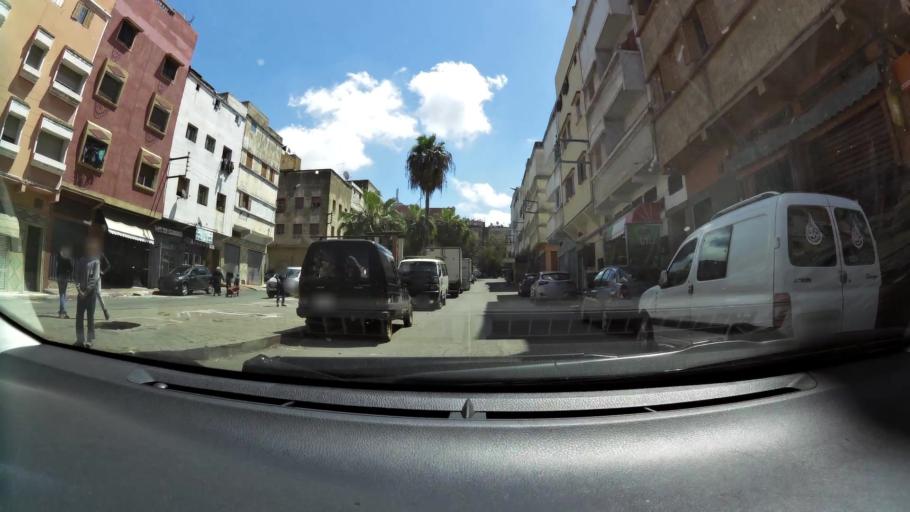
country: MA
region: Grand Casablanca
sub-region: Casablanca
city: Casablanca
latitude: 33.5620
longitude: -7.5697
